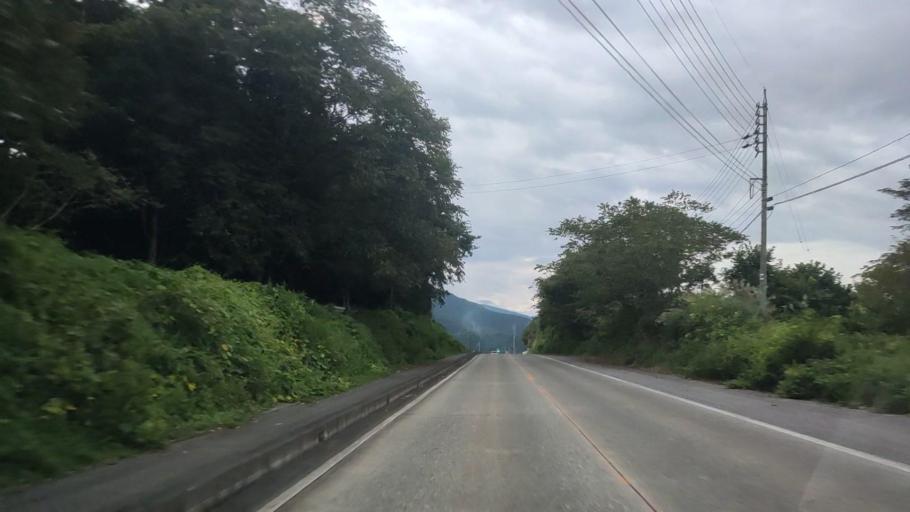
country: JP
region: Nagano
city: Iiyama
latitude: 36.8884
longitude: 138.4089
